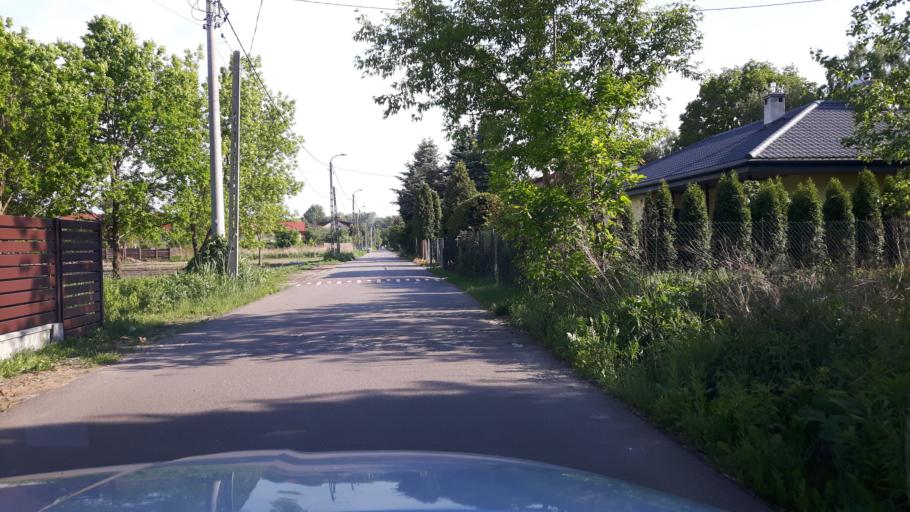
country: PL
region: Masovian Voivodeship
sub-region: Warszawa
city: Praga Poludnie
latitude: 52.2574
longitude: 21.1207
